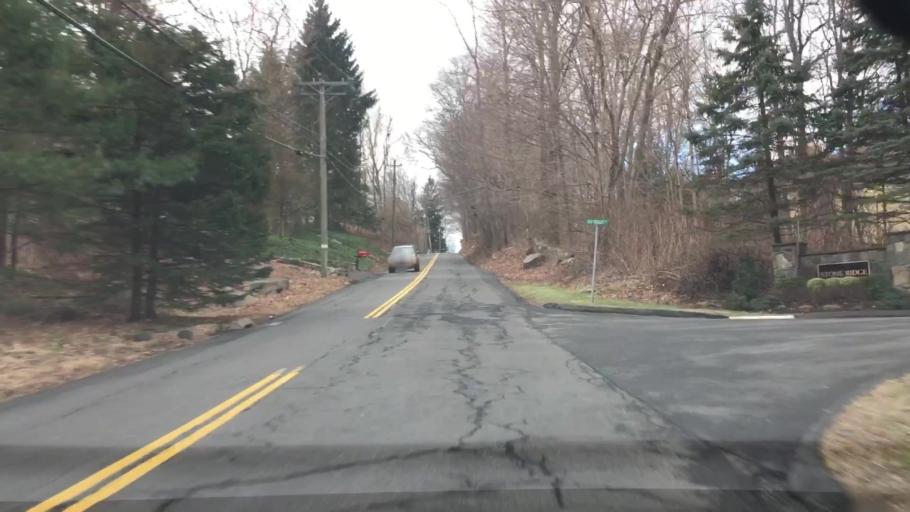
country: US
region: New York
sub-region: Putnam County
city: Peach Lake
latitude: 41.3624
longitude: -73.5122
